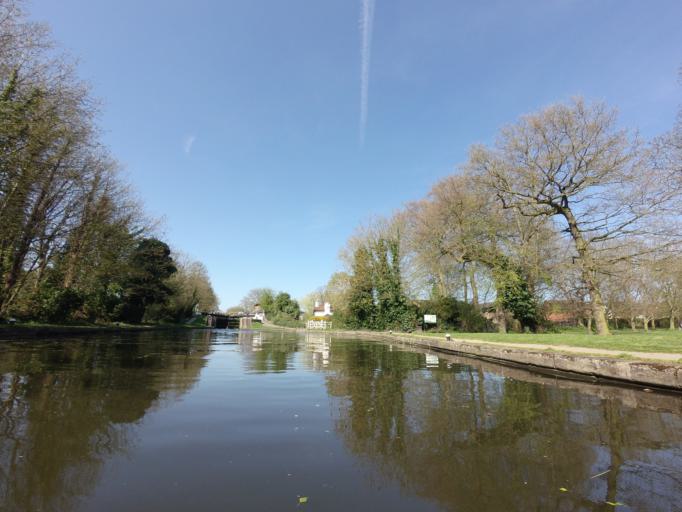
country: GB
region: England
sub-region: Greater London
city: Uxbridge
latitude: 51.5282
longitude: -0.4856
